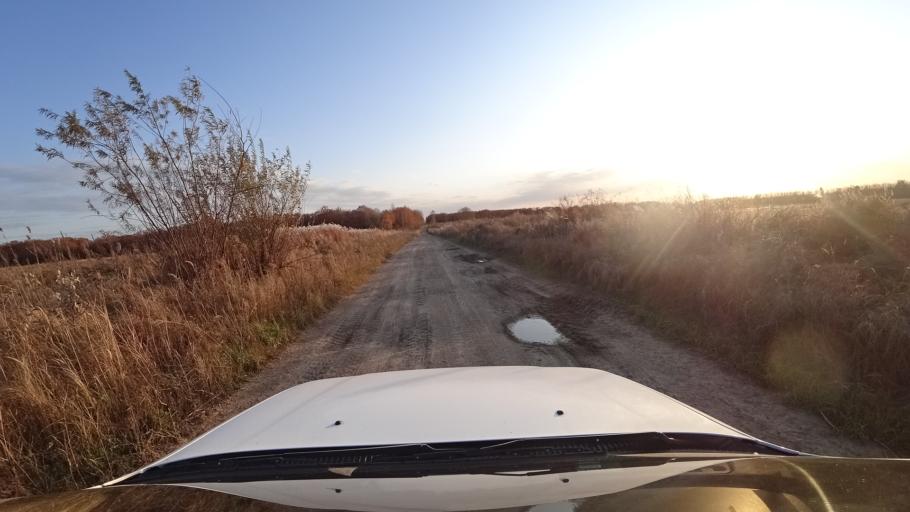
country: RU
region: Primorskiy
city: Lazo
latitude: 45.8087
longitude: 133.6068
